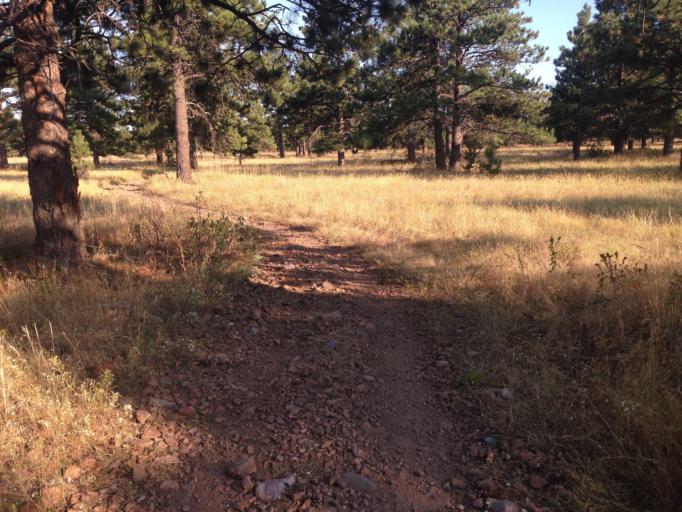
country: US
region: Colorado
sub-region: Boulder County
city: Superior
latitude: 39.9146
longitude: -105.2581
